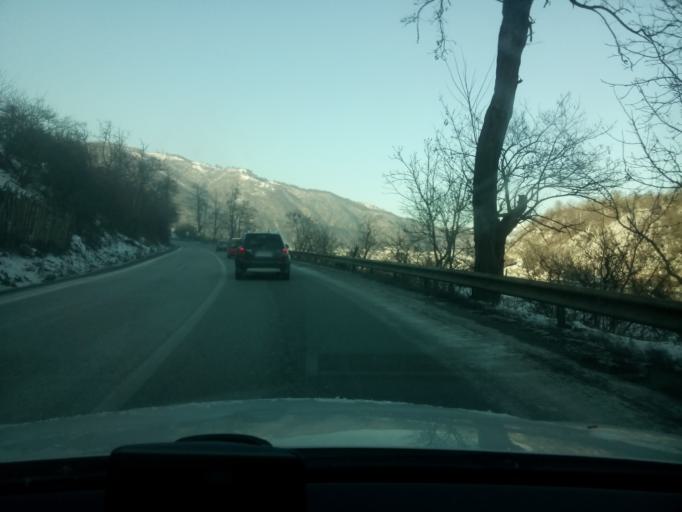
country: RO
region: Valcea
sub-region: Comuna Racovita
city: Racovita
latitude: 45.4143
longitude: 24.2943
